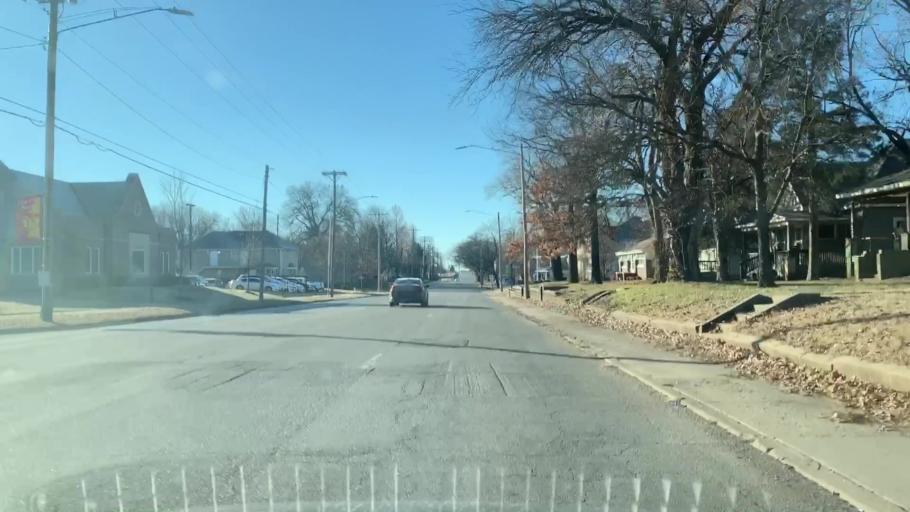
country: US
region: Kansas
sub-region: Crawford County
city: Pittsburg
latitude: 37.3904
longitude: -94.7052
